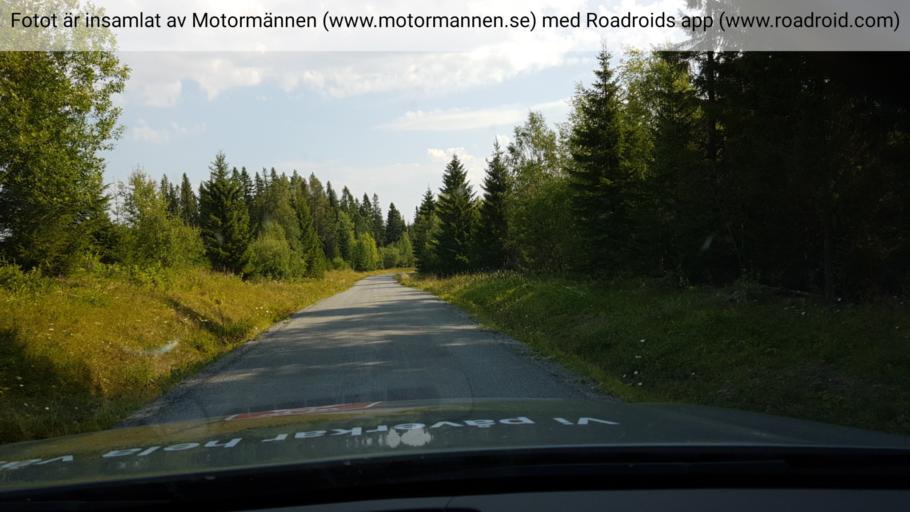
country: SE
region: Jaemtland
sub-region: OEstersunds Kommun
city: Ostersund
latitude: 63.1226
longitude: 14.6302
